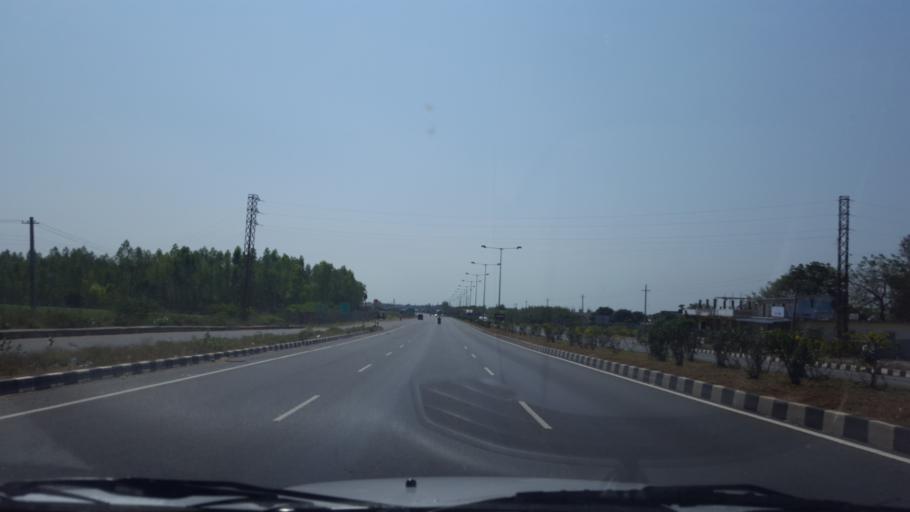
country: IN
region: Andhra Pradesh
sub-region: Prakasam
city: Ongole
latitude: 15.6544
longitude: 80.0152
